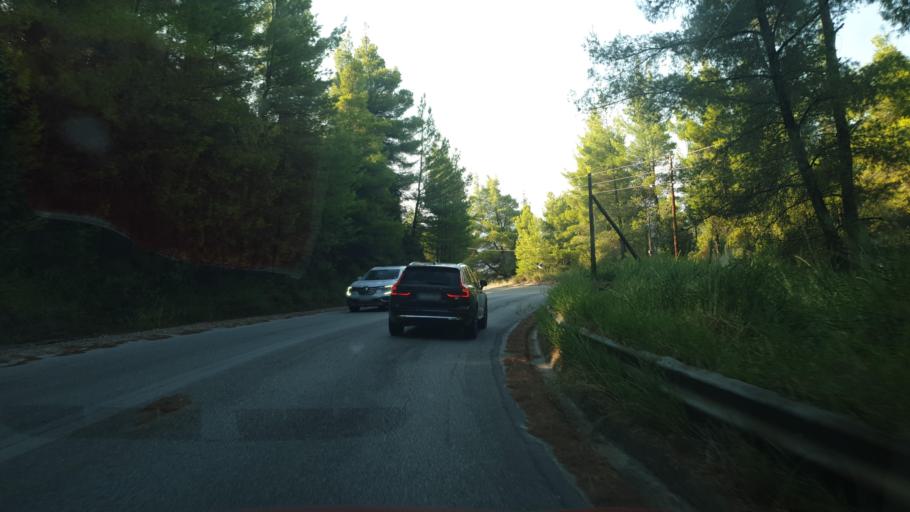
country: GR
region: Central Macedonia
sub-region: Nomos Chalkidikis
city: Neos Marmaras
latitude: 40.1754
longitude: 23.8393
